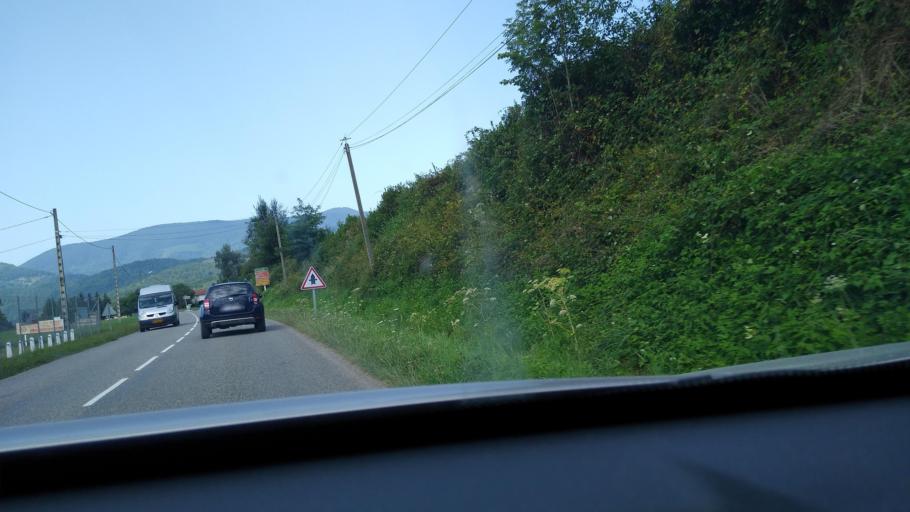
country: FR
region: Midi-Pyrenees
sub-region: Departement de l'Ariege
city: Saint-Girons
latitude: 42.8709
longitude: 1.2108
